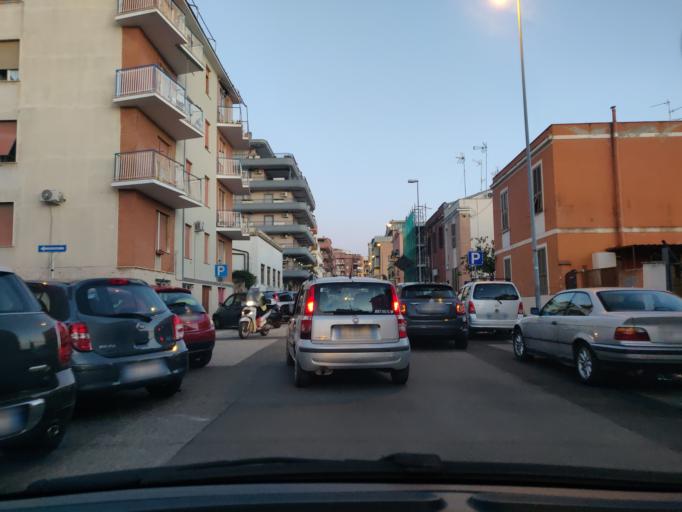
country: IT
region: Latium
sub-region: Citta metropolitana di Roma Capitale
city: Civitavecchia
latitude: 42.0894
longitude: 11.8002
